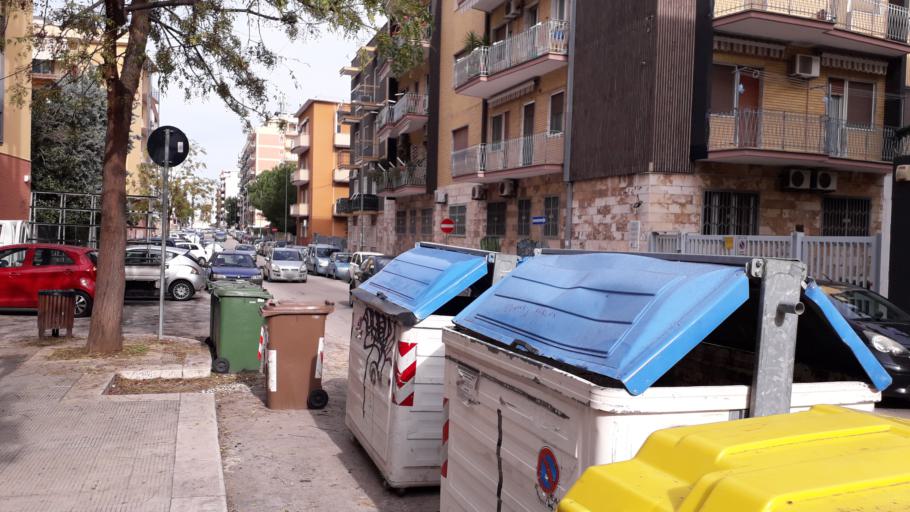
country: IT
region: Apulia
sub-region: Provincia di Bari
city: Bari
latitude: 41.1089
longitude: 16.8756
